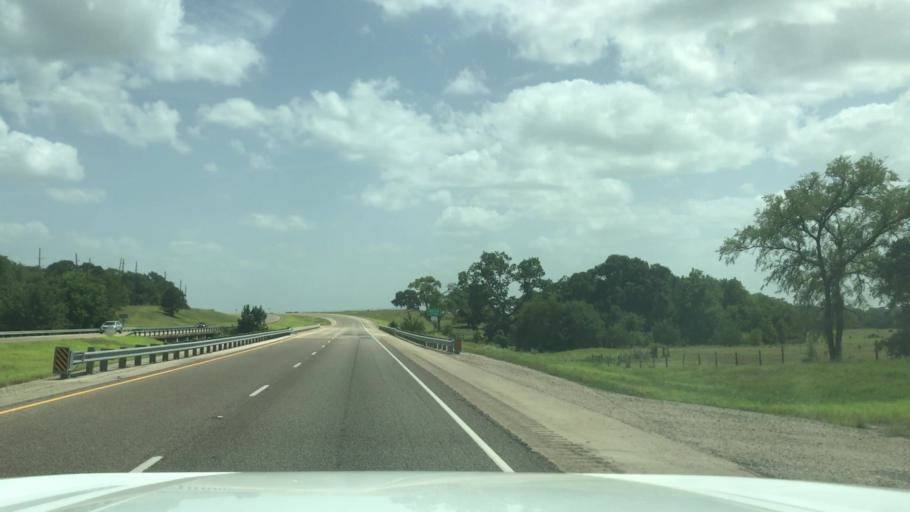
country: US
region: Texas
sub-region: Robertson County
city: Calvert
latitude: 31.0113
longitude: -96.7034
